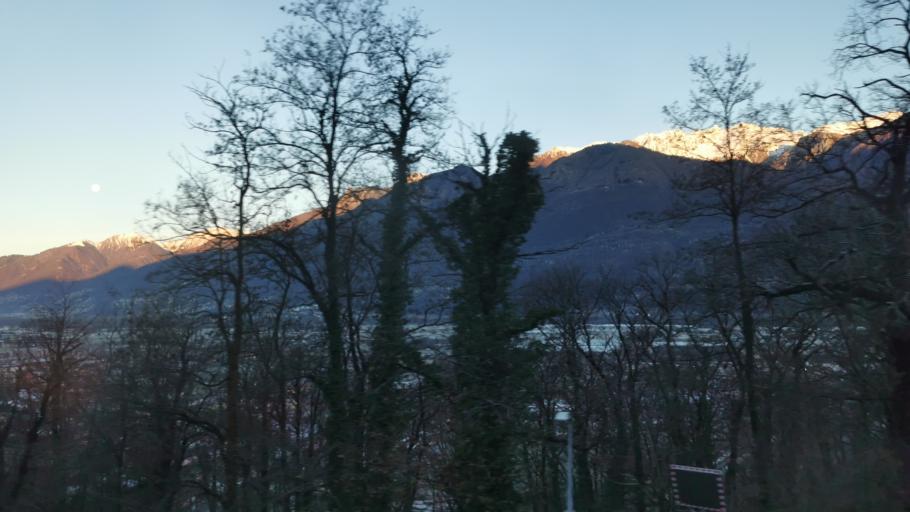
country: CH
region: Ticino
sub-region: Bellinzona District
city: Camorino
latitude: 46.1550
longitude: 8.9873
